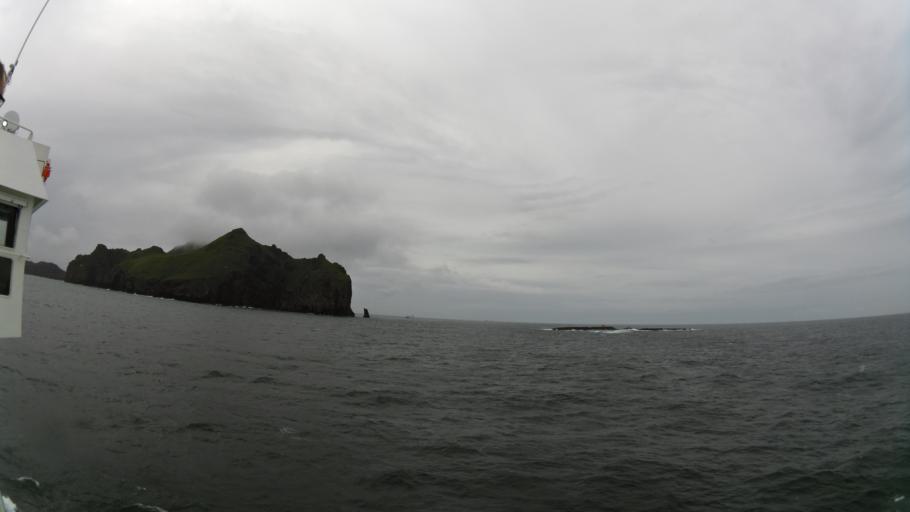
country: IS
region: South
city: Vestmannaeyjar
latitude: 63.4569
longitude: -20.2247
